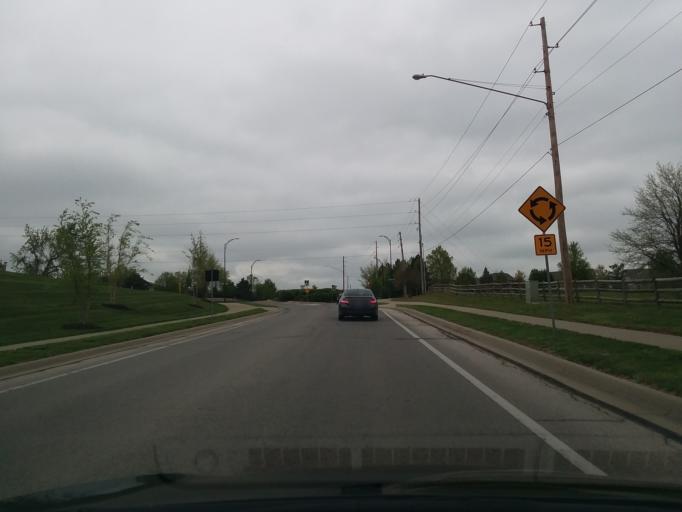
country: US
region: Kansas
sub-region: Douglas County
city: Lawrence
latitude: 38.9851
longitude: -95.2882
